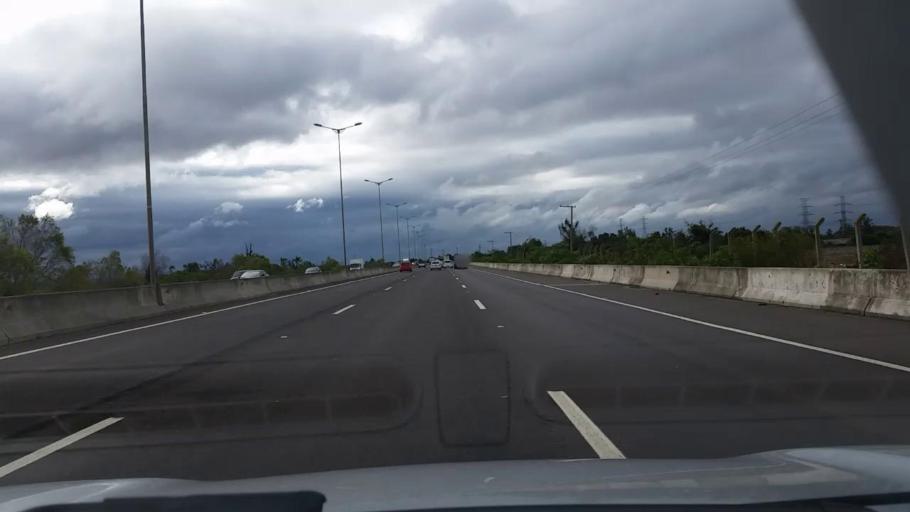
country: BR
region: Rio Grande do Sul
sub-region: Canoas
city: Canoas
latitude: -29.9470
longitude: -51.2040
